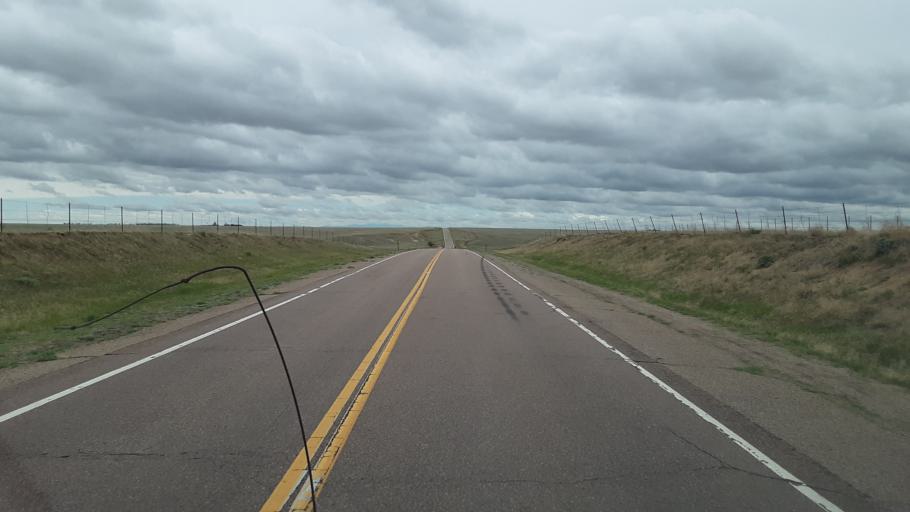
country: US
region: Colorado
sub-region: Lincoln County
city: Limon
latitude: 38.8390
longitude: -103.8994
